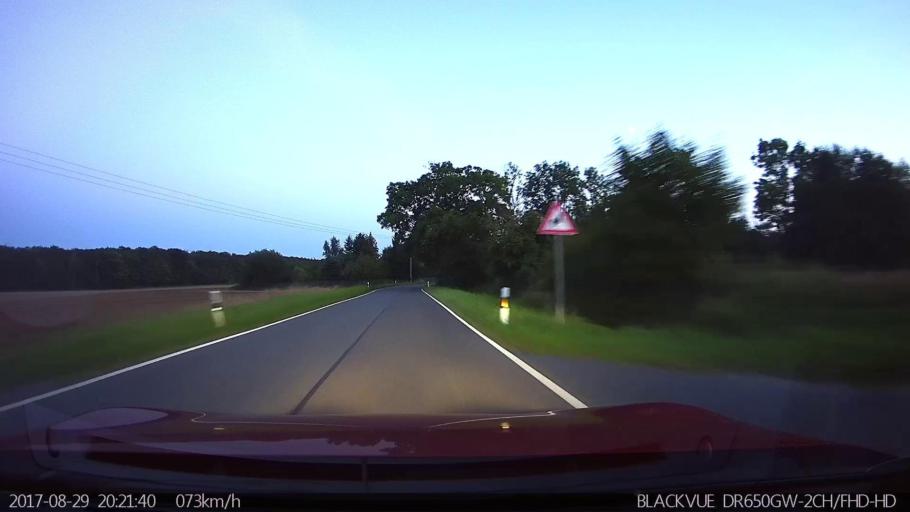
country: DE
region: Mecklenburg-Vorpommern
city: Velgast
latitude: 54.2468
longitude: 12.8249
